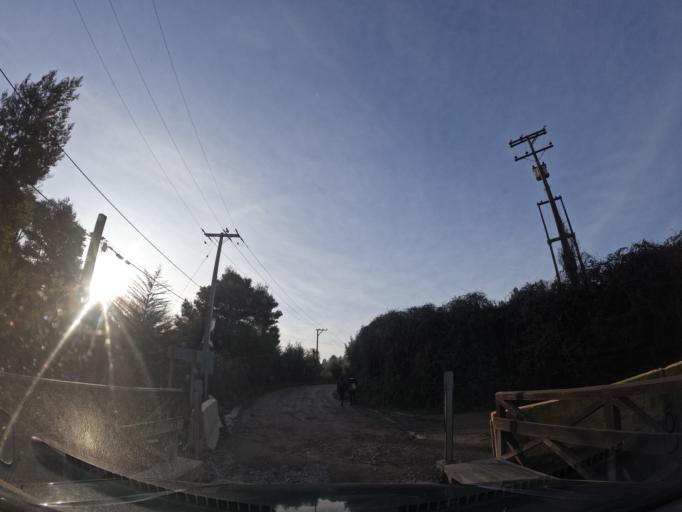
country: CL
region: Biobio
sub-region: Provincia de Concepcion
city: Concepcion
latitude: -36.8531
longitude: -73.0056
